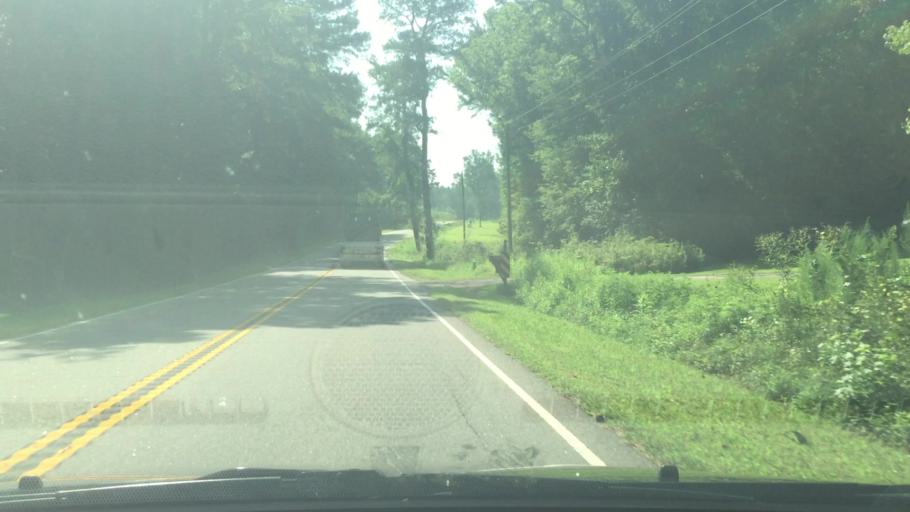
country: US
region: Virginia
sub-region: Sussex County
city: Sussex
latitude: 37.0271
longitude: -77.2937
